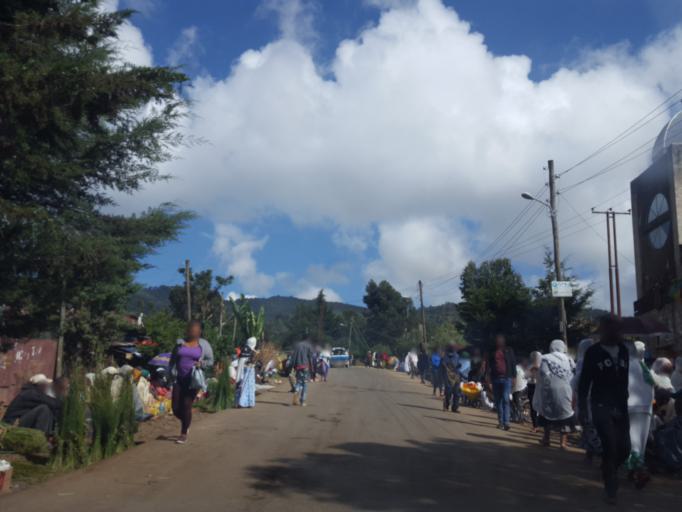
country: ET
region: Adis Abeba
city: Addis Ababa
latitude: 9.0698
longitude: 38.7607
